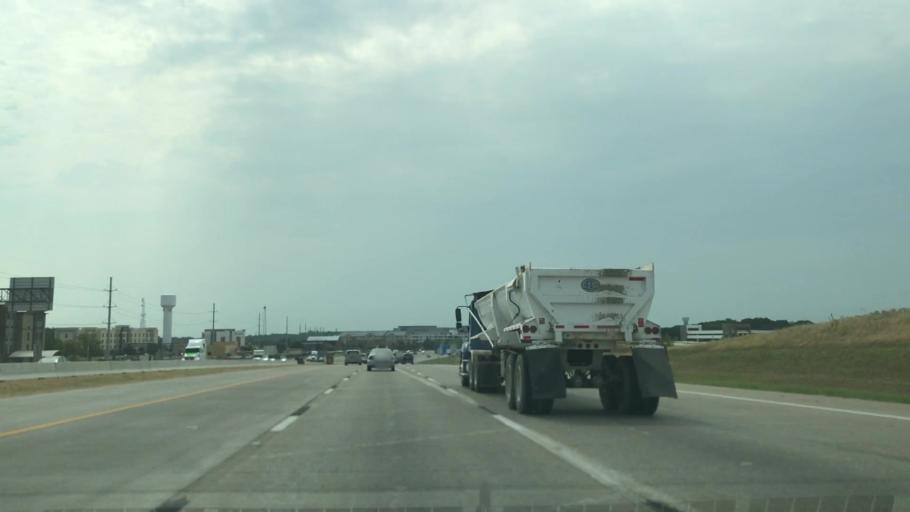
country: US
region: Texas
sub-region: Denton County
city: Trophy Club
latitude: 32.9880
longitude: -97.1772
